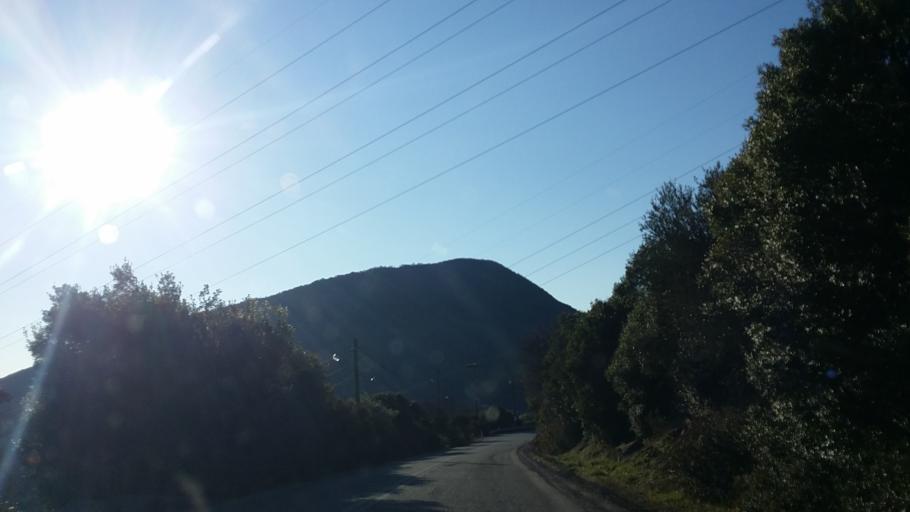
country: GR
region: West Greece
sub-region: Nomos Aitolias kai Akarnanias
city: Neapolis
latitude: 38.7962
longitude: 21.4575
